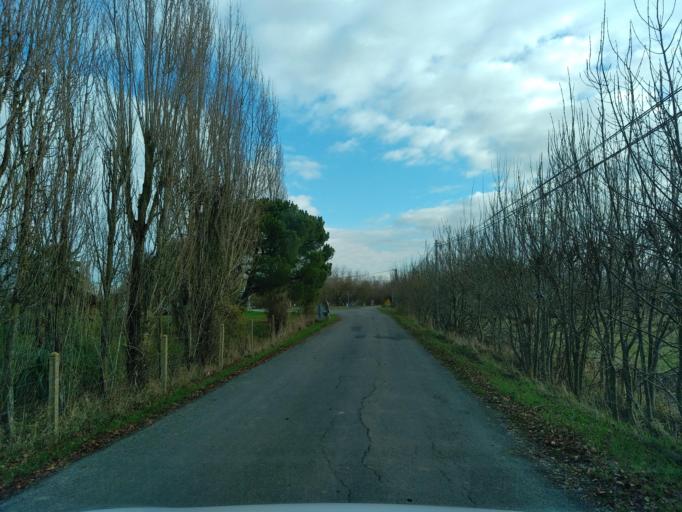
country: FR
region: Pays de la Loire
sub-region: Departement de la Vendee
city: Maillezais
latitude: 46.3179
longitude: -0.7786
